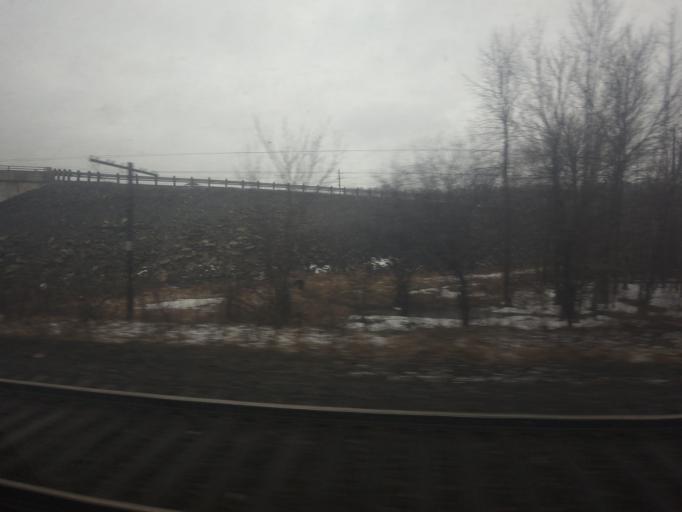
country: CA
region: Ontario
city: Kingston
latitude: 44.2961
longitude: -76.4256
